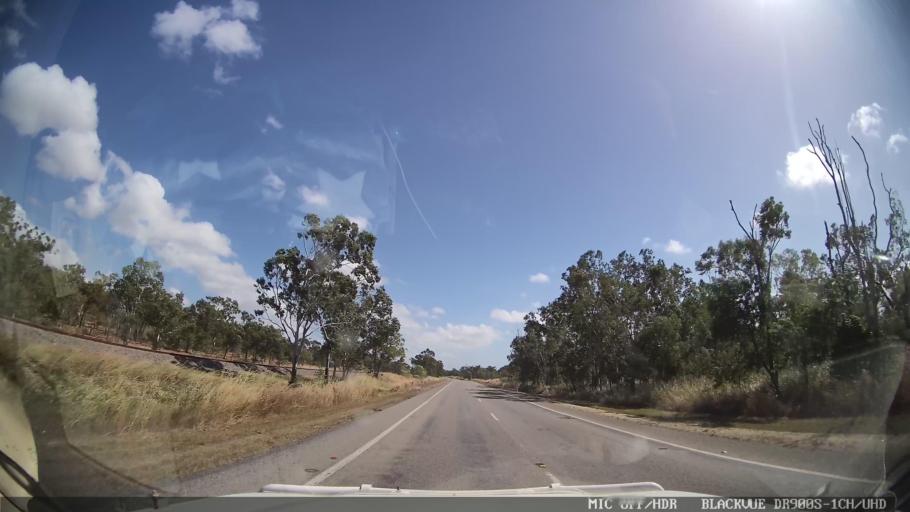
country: AU
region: Queensland
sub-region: Whitsunday
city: Bowen
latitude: -20.1798
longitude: 148.3497
